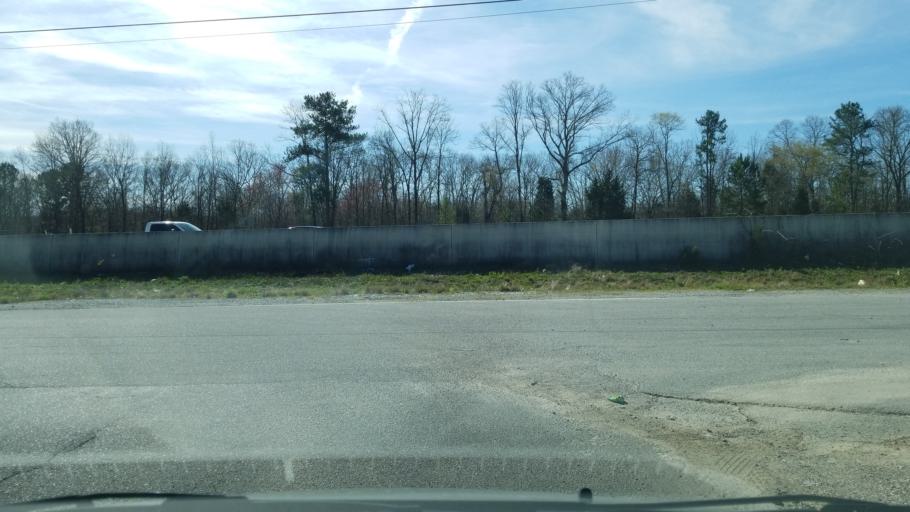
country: US
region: Tennessee
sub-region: Hamilton County
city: Collegedale
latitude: 35.0812
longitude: -85.0864
